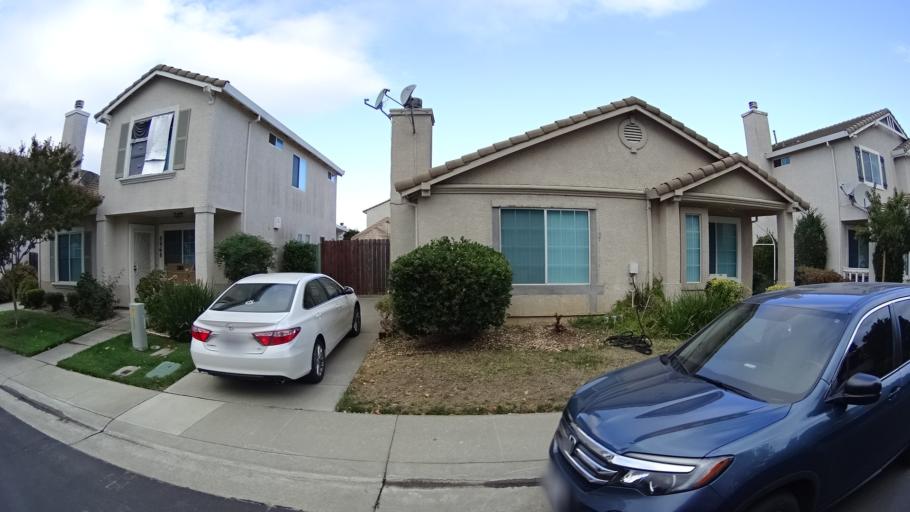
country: US
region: California
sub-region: Sacramento County
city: Laguna
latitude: 38.4316
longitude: -121.4228
